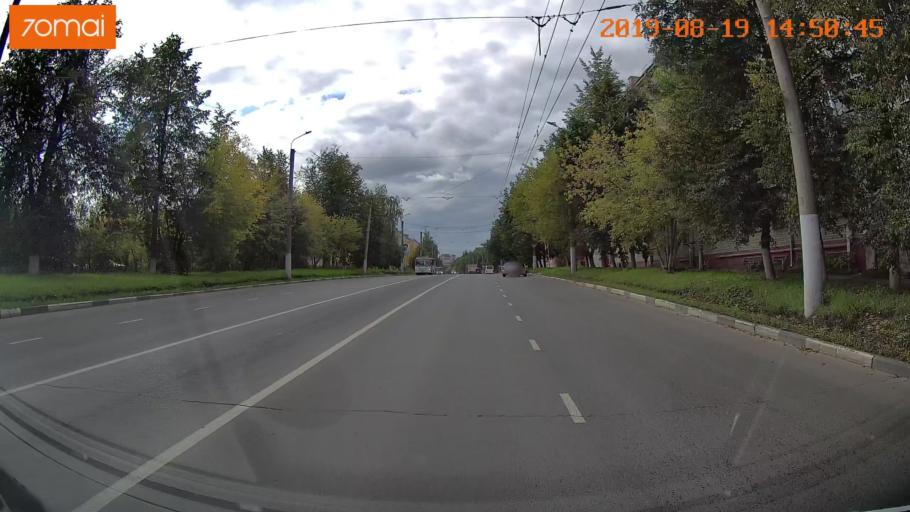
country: RU
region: Ivanovo
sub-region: Gorod Ivanovo
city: Ivanovo
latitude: 56.9943
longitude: 41.0090
